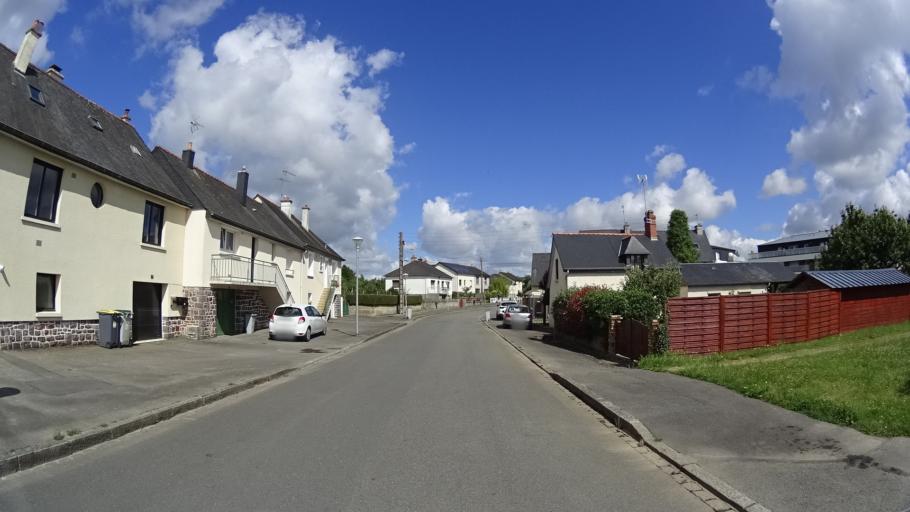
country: FR
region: Brittany
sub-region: Departement d'Ille-et-Vilaine
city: Le Rheu
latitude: 48.1230
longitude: -1.8092
